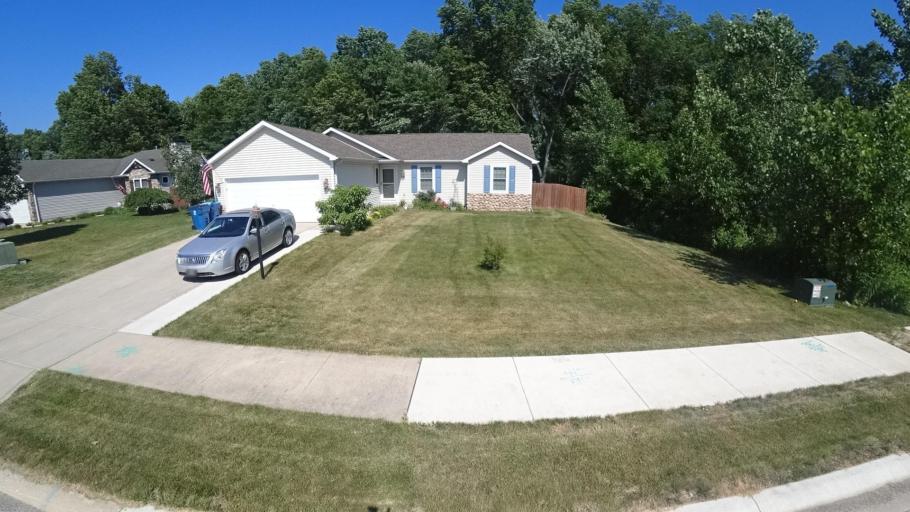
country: US
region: Indiana
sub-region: Porter County
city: Burns Harbor
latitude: 41.5996
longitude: -87.1076
